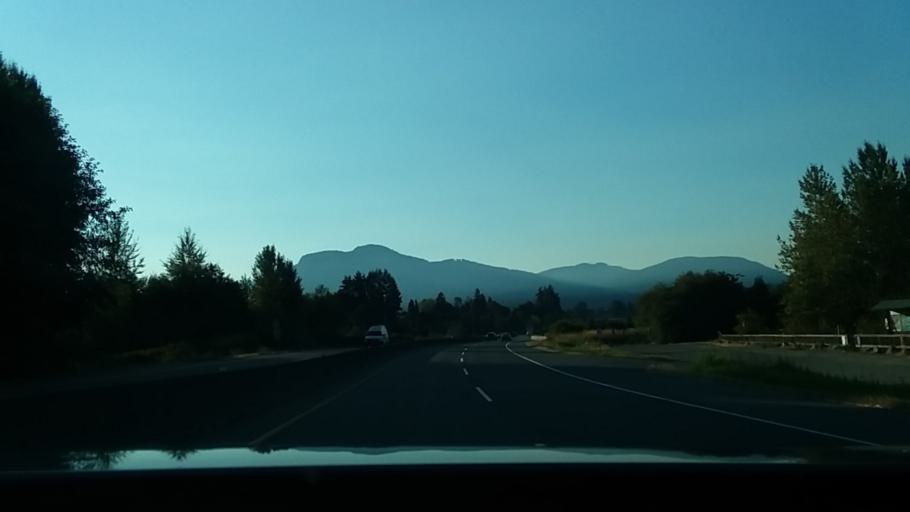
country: CA
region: British Columbia
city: Duncan
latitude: 48.7892
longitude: -123.7102
